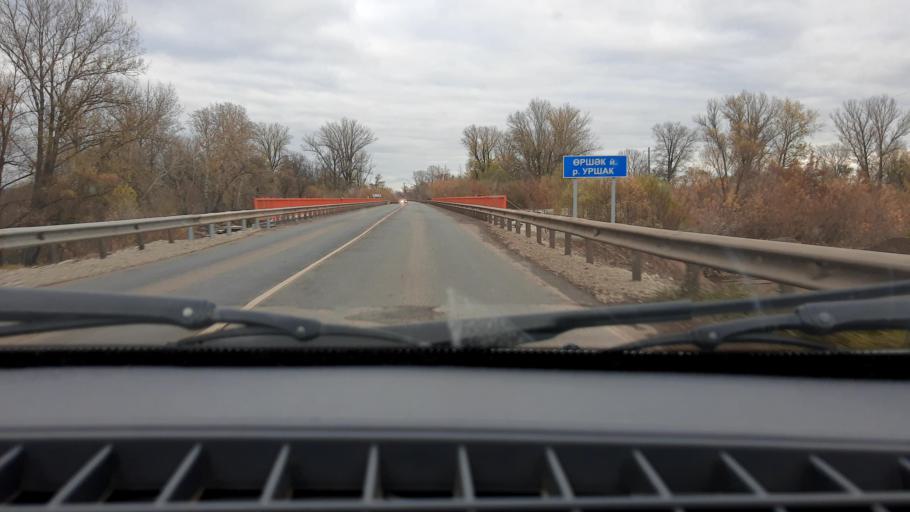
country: RU
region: Bashkortostan
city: Ufa
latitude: 54.5697
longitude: 55.9744
